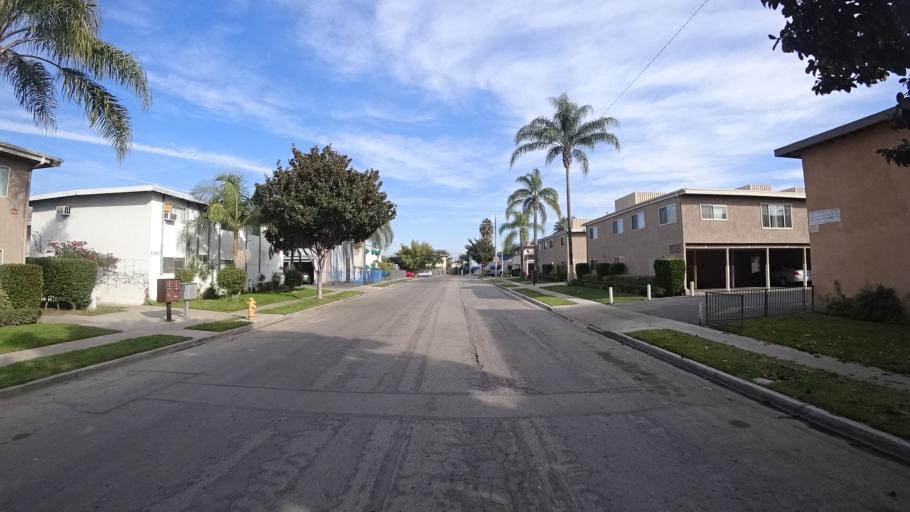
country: US
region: California
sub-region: Orange County
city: Garden Grove
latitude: 33.7566
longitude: -117.9088
